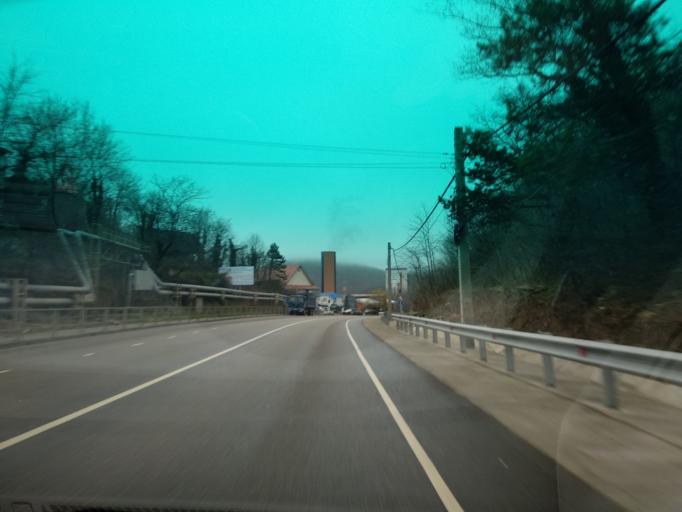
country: RU
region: Krasnodarskiy
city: Tuapse
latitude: 44.1115
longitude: 39.0717
